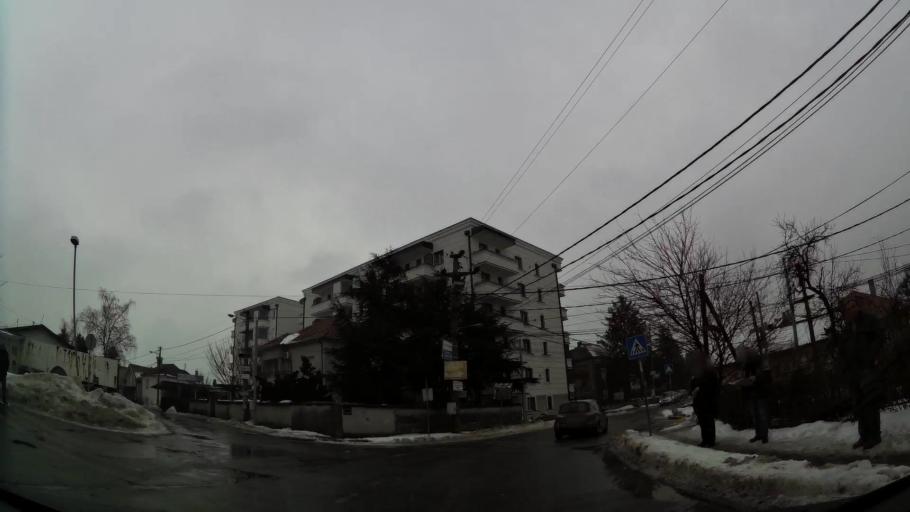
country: RS
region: Central Serbia
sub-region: Belgrade
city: Zvezdara
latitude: 44.7745
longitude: 20.5360
